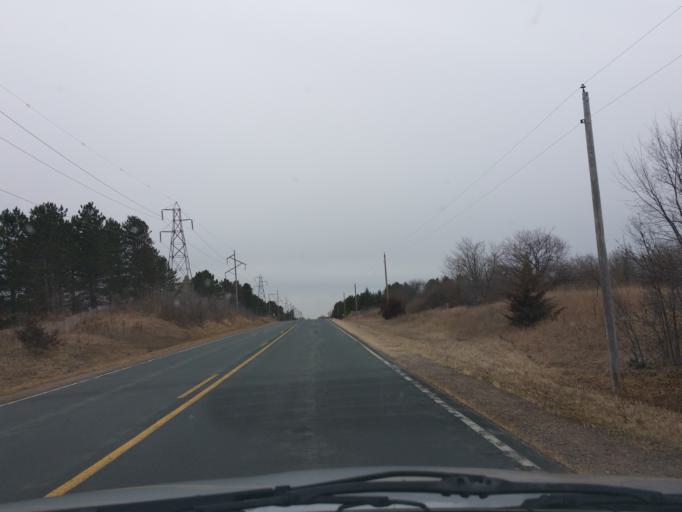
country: US
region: Wisconsin
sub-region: Saint Croix County
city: Roberts
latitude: 45.0357
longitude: -92.6163
